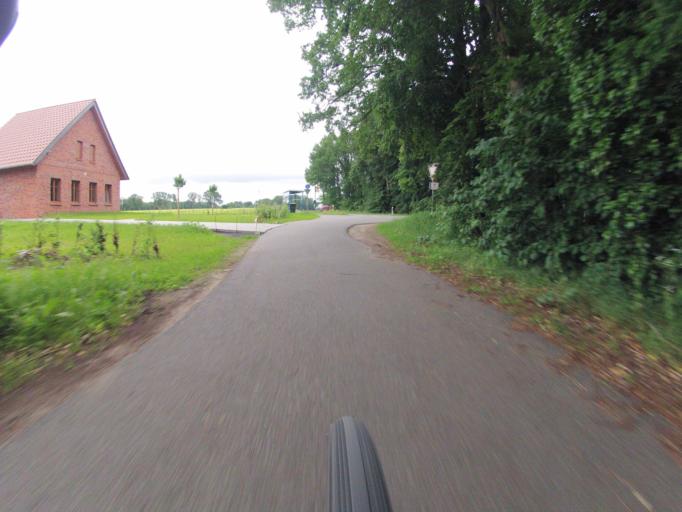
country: DE
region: North Rhine-Westphalia
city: Emsdetten
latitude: 52.2011
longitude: 7.5521
